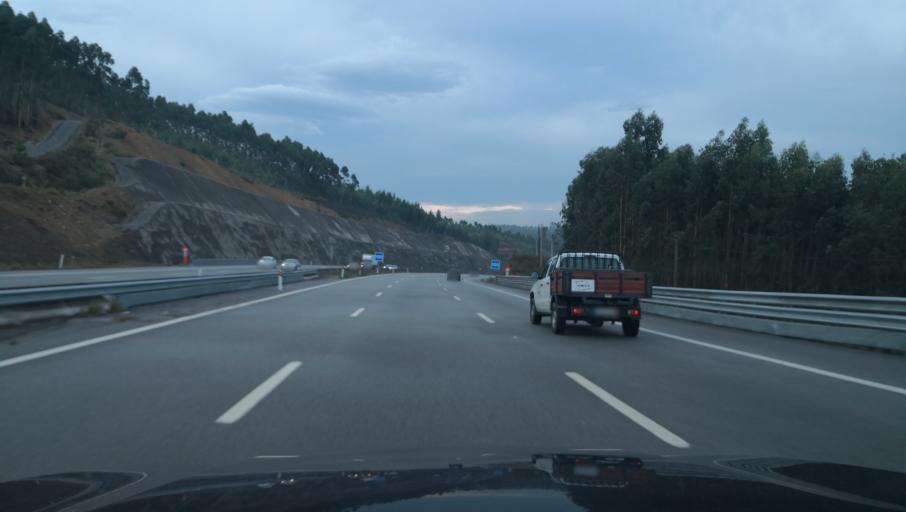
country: PT
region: Porto
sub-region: Paredes
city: Recarei
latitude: 41.1149
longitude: -8.4324
